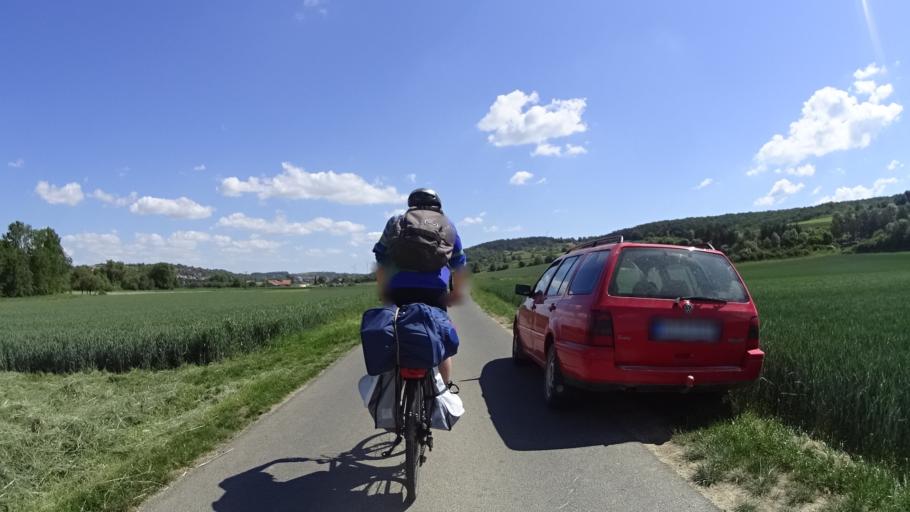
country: DE
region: Bavaria
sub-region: Regierungsbezirk Unterfranken
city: Rottingen
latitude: 49.5006
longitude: 9.9611
